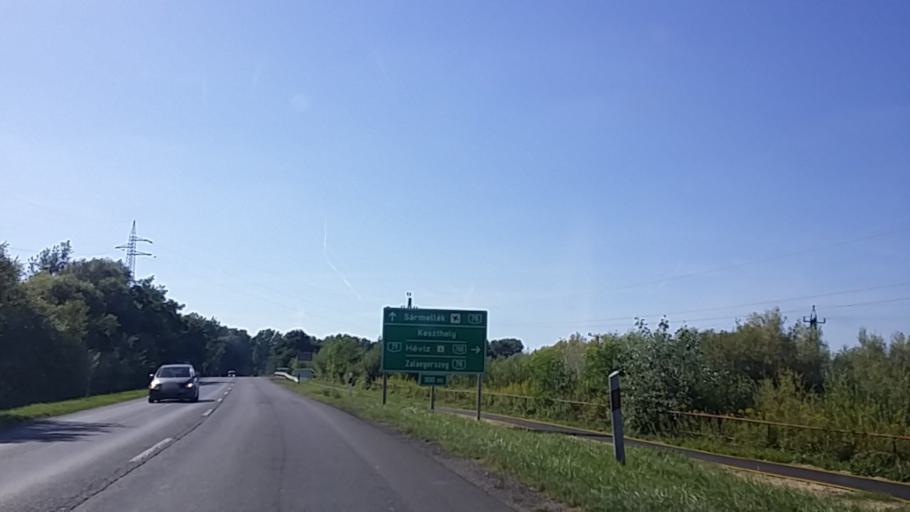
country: HU
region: Somogy
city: Balatonbereny
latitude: 46.7022
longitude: 17.2601
